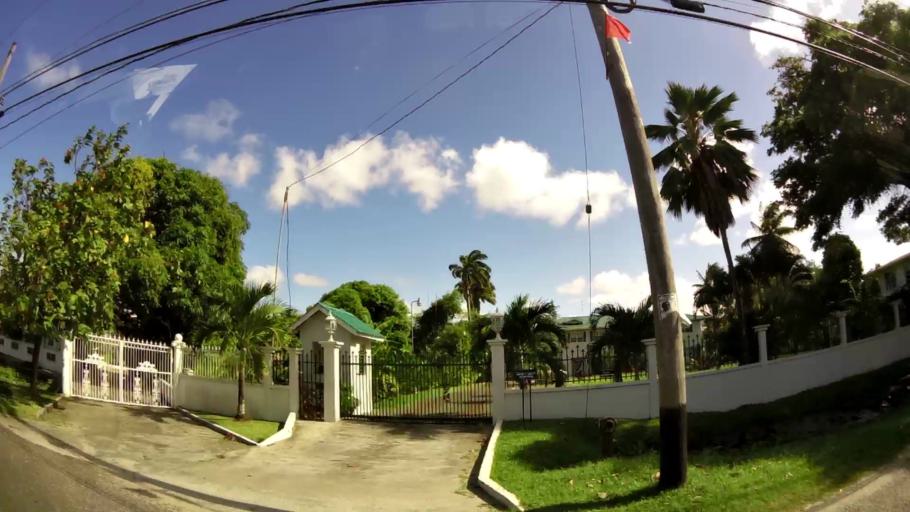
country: GY
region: Demerara-Mahaica
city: Georgetown
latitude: 6.8223
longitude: -58.1286
